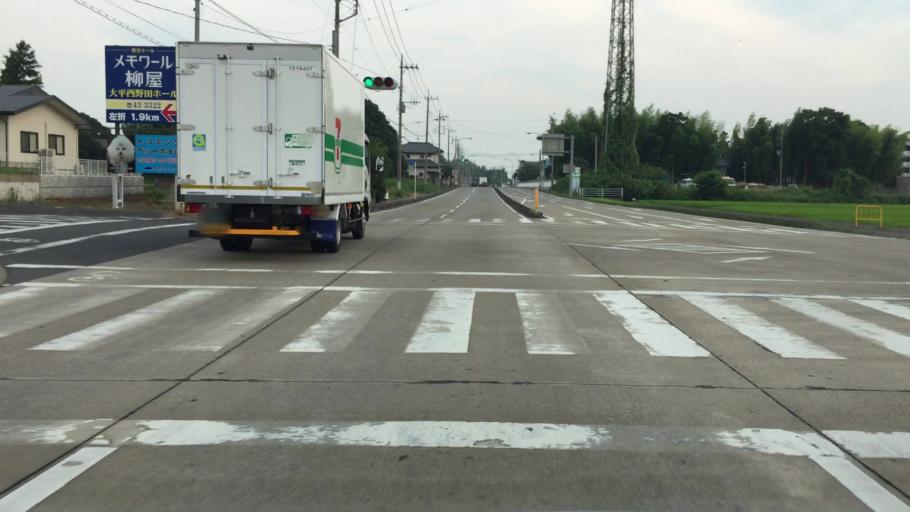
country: JP
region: Tochigi
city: Tochigi
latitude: 36.3389
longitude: 139.6956
